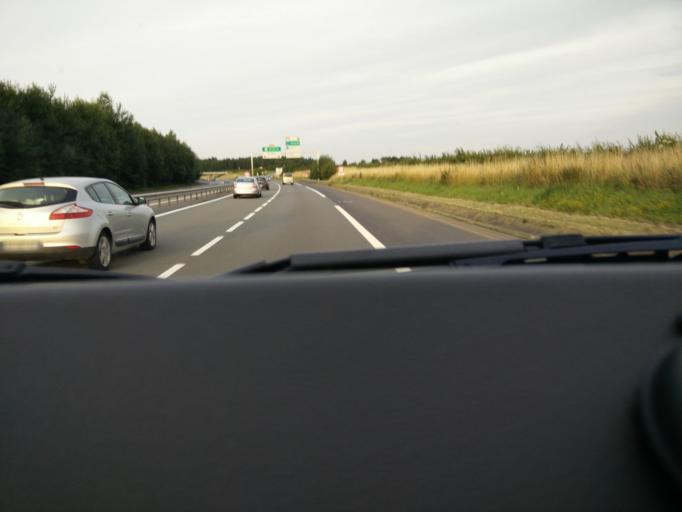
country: FR
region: Nord-Pas-de-Calais
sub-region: Departement du Nord
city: Gommegnies
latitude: 50.3013
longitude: 3.7155
